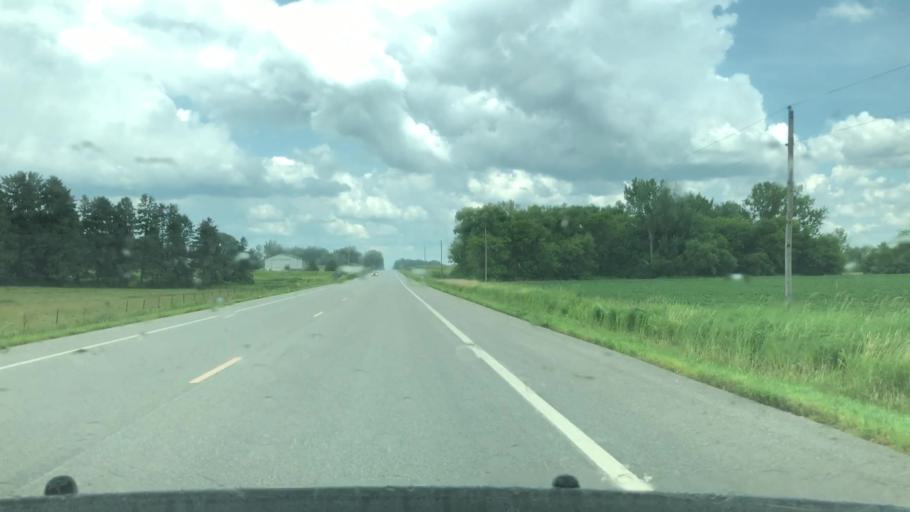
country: US
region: Minnesota
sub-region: Olmsted County
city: Stewartville
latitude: 43.8973
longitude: -92.5284
